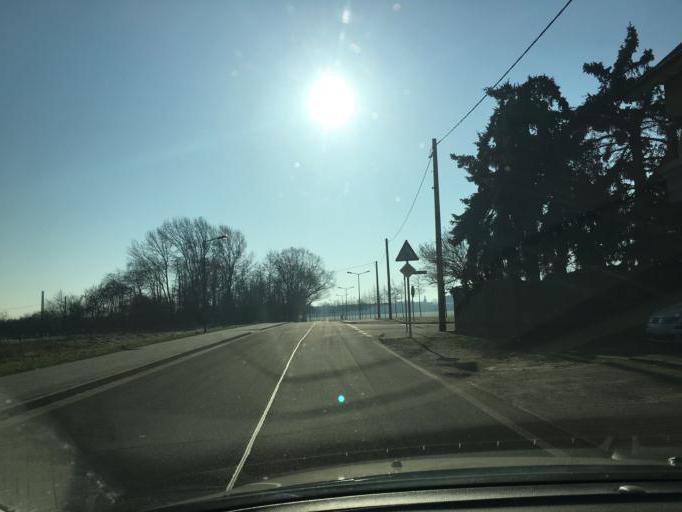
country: DE
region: Saxony
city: Grossposna
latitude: 51.2921
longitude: 12.4560
